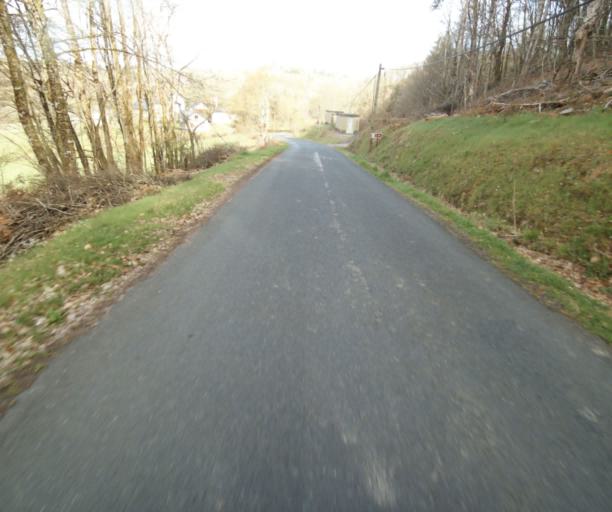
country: FR
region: Limousin
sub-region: Departement de la Correze
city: Correze
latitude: 45.3407
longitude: 1.8232
